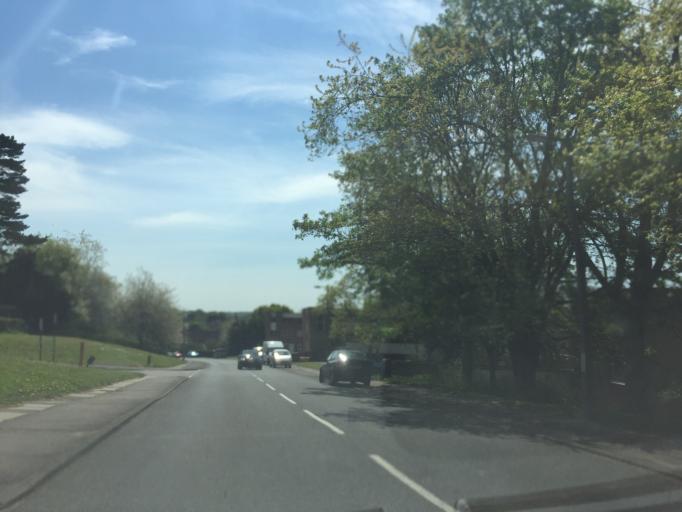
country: GB
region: England
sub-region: Essex
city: Harlow
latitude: 51.7643
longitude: 0.0845
